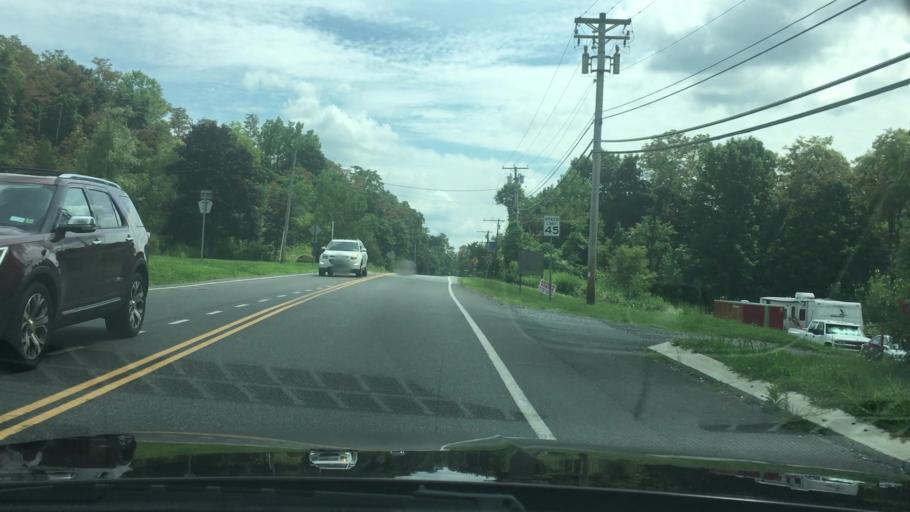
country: US
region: New York
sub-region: Dutchess County
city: Red Oaks Mill
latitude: 41.6586
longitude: -73.8479
